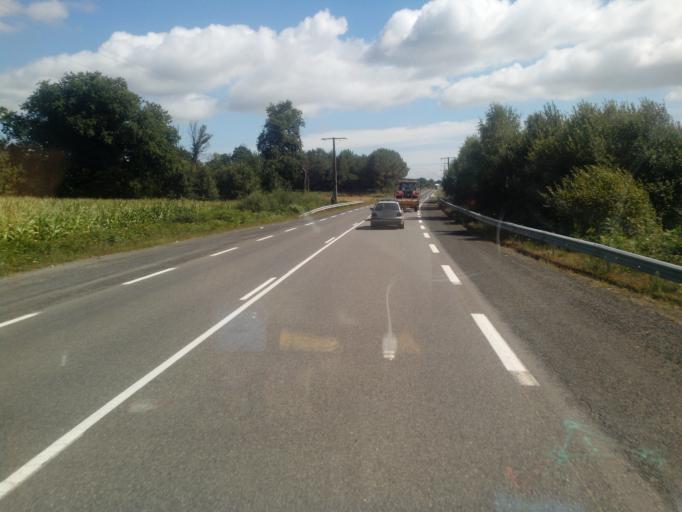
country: FR
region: Brittany
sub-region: Departement du Morbihan
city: Limerzel
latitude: 47.6094
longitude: -2.3880
